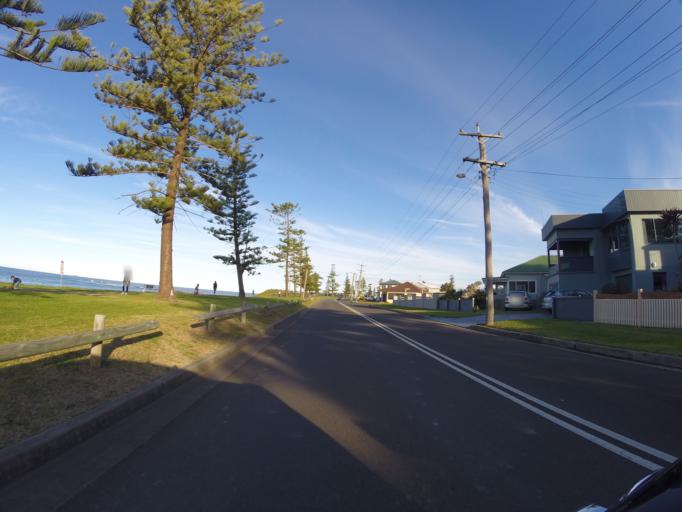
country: AU
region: New South Wales
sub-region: Wollongong
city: Bulli
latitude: -34.3369
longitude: 150.9244
